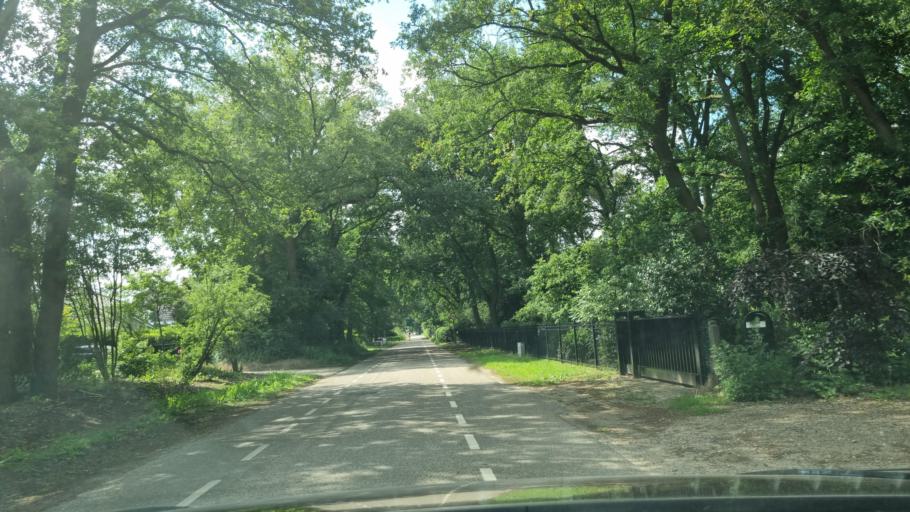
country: NL
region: Gelderland
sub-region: Gemeente Groesbeek
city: Bredeweg
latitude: 51.7260
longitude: 5.9232
